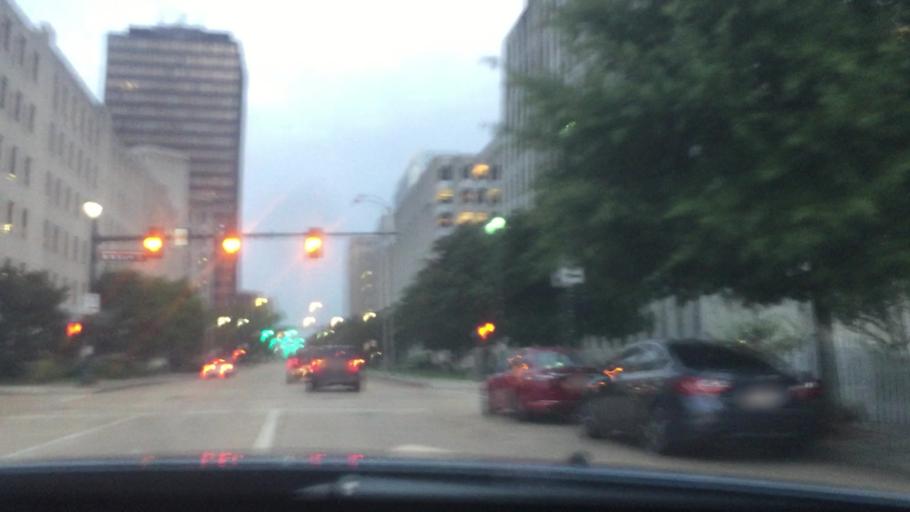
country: US
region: Louisiana
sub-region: West Baton Rouge Parish
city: Port Allen
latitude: 30.4526
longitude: -91.1845
